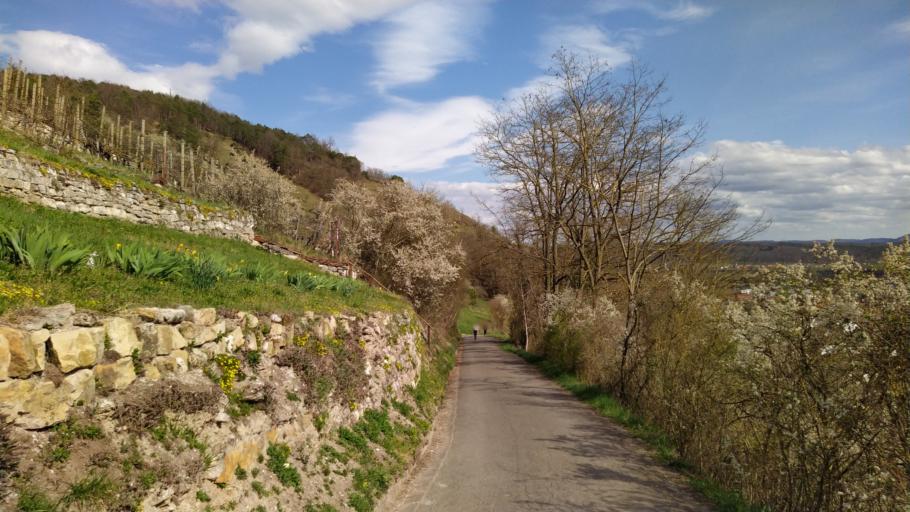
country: DE
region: Baden-Wuerttemberg
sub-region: Tuebingen Region
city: Rottenburg
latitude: 48.5050
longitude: 8.9908
